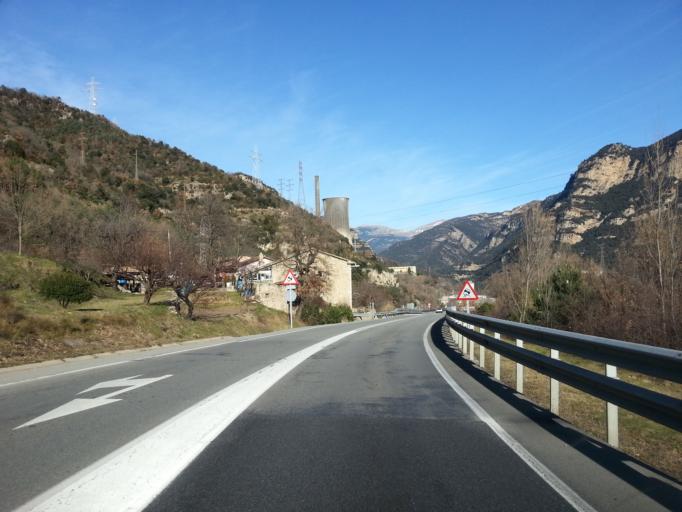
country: ES
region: Catalonia
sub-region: Provincia de Barcelona
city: Vallcebre
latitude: 42.1655
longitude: 1.8553
